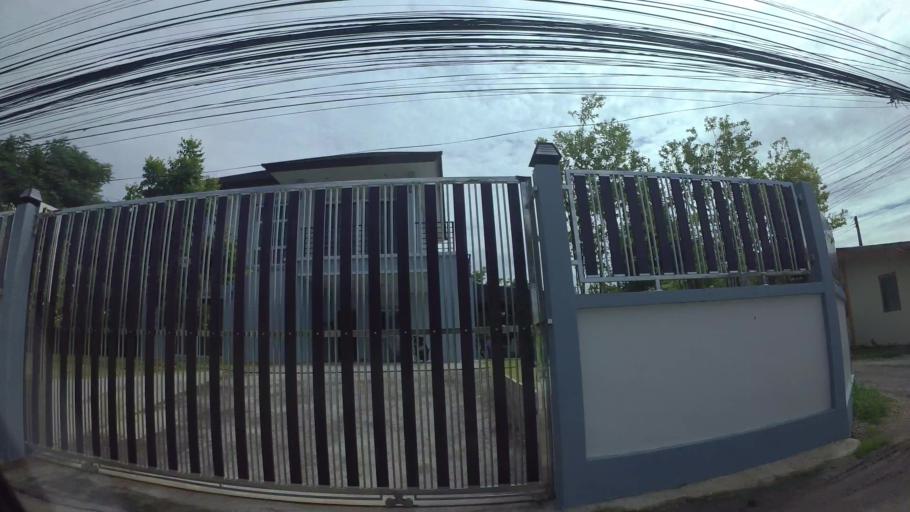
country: TH
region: Rayong
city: Rayong
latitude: 12.6664
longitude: 101.2830
